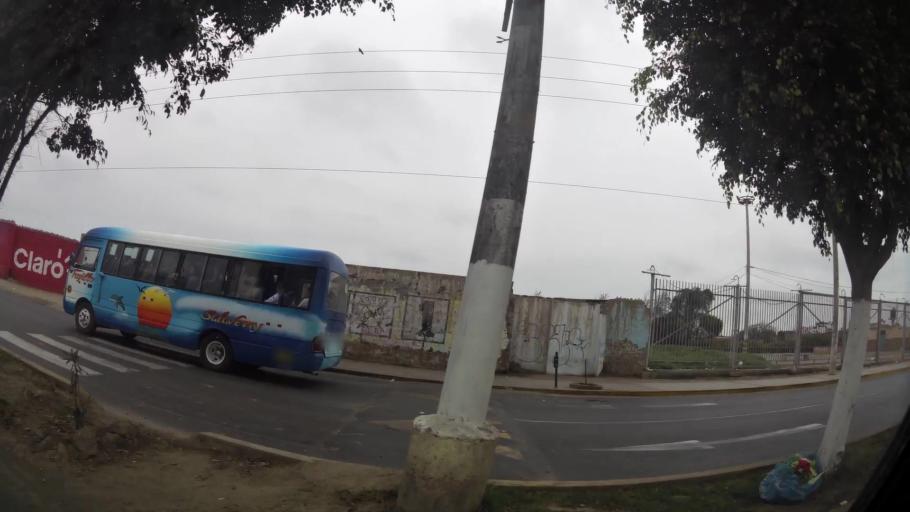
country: PE
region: La Libertad
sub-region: Provincia de Trujillo
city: Trujillo
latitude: -8.1286
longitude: -79.0217
